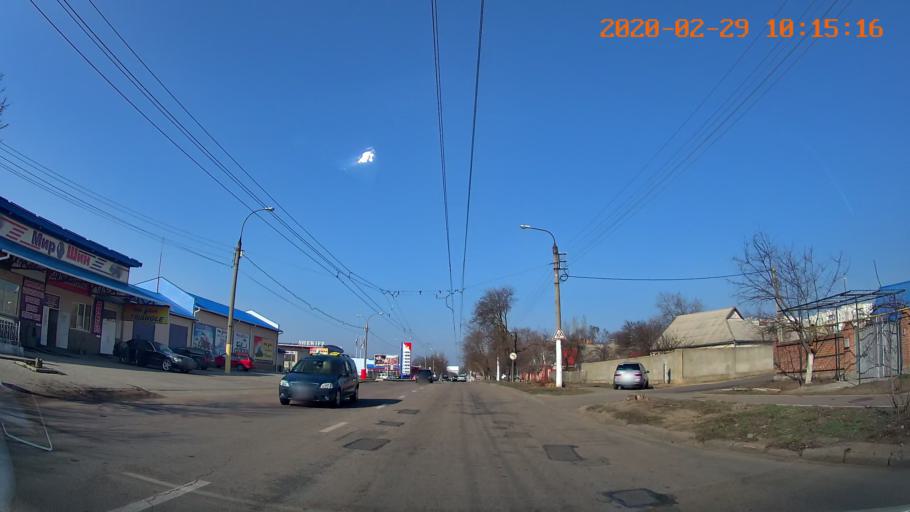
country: MD
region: Telenesti
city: Tiraspolul Nou
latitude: 46.8526
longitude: 29.6390
